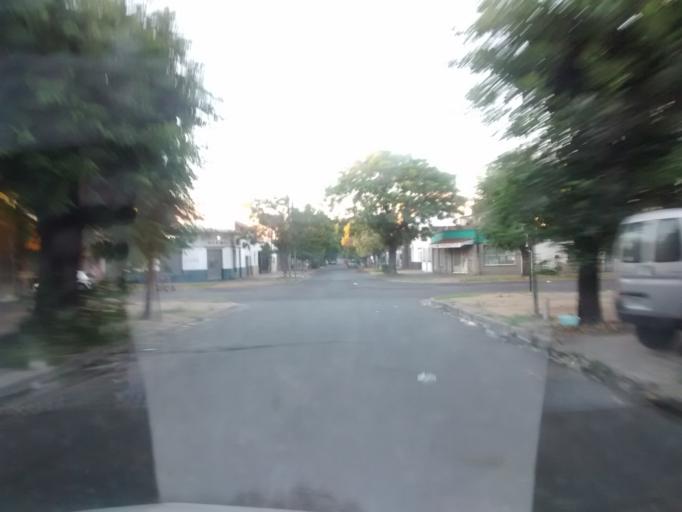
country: AR
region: Buenos Aires
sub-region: Partido de La Plata
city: La Plata
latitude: -34.9443
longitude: -57.9506
